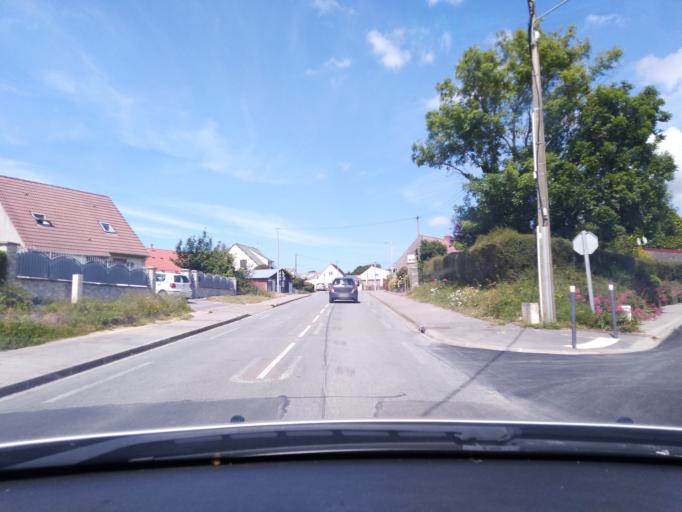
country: FR
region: Nord-Pas-de-Calais
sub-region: Departement du Pas-de-Calais
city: Ferques
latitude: 50.8330
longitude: 1.7594
